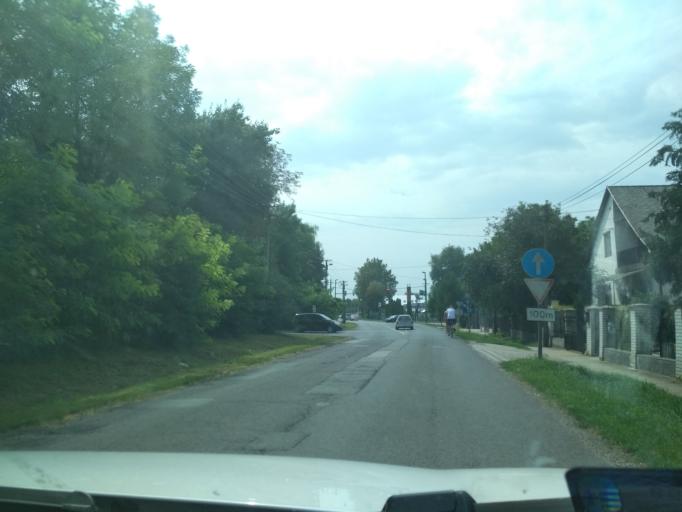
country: HU
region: Jasz-Nagykun-Szolnok
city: Tiszafured
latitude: 47.6089
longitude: 20.7621
